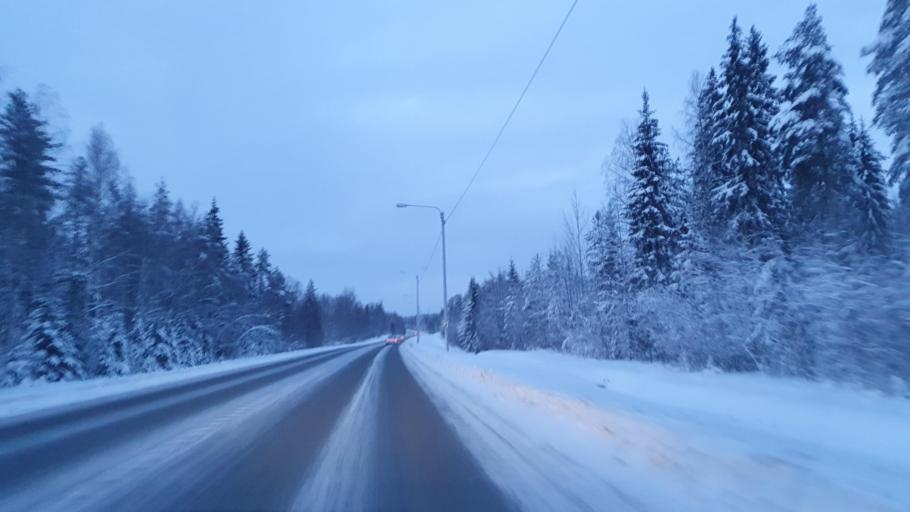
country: FI
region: Northern Ostrobothnia
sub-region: Oulu
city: Tyrnaevae
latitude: 64.9172
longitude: 25.7578
